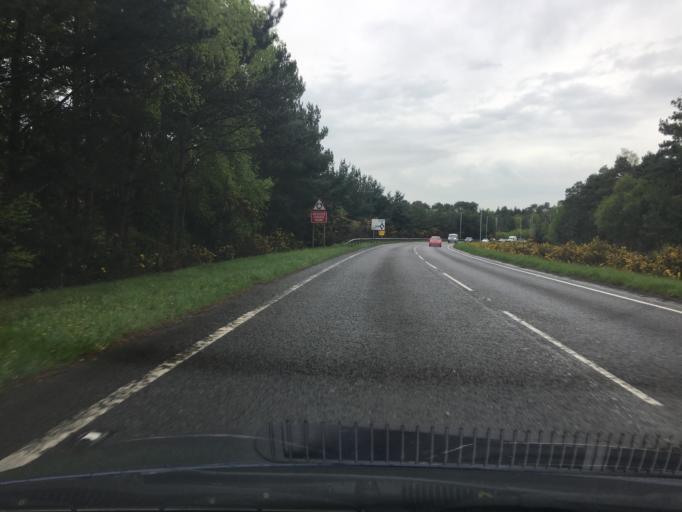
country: GB
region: England
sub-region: Bracknell Forest
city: Crowthorne
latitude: 51.3797
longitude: -0.7724
